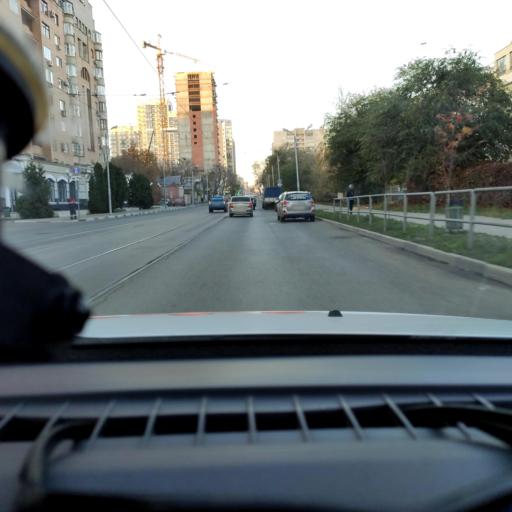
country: RU
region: Samara
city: Samara
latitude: 53.2058
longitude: 50.1216
